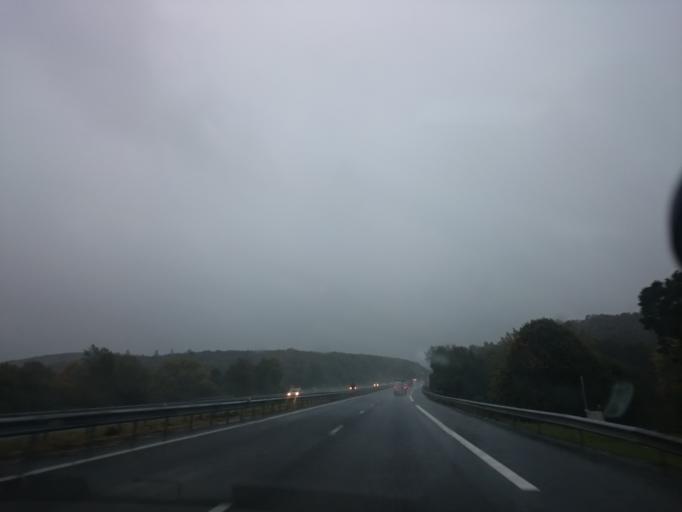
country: FR
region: Brittany
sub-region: Departement du Finistere
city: Le Faou
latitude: 48.2973
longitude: -4.1713
